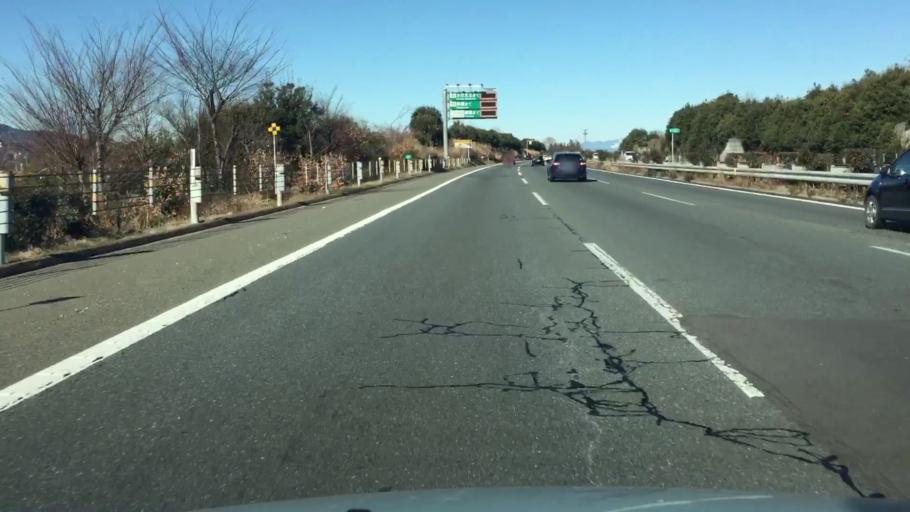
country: JP
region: Saitama
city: Yorii
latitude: 36.1331
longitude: 139.2331
